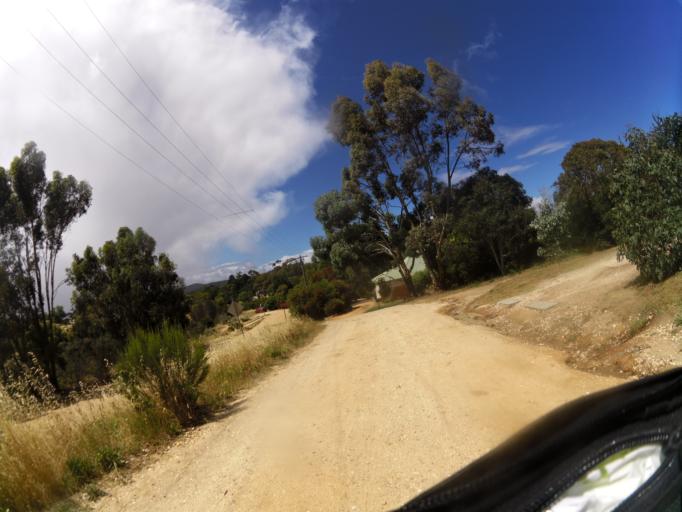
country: AU
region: Victoria
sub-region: Mount Alexander
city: Castlemaine
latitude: -37.0680
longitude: 144.2276
